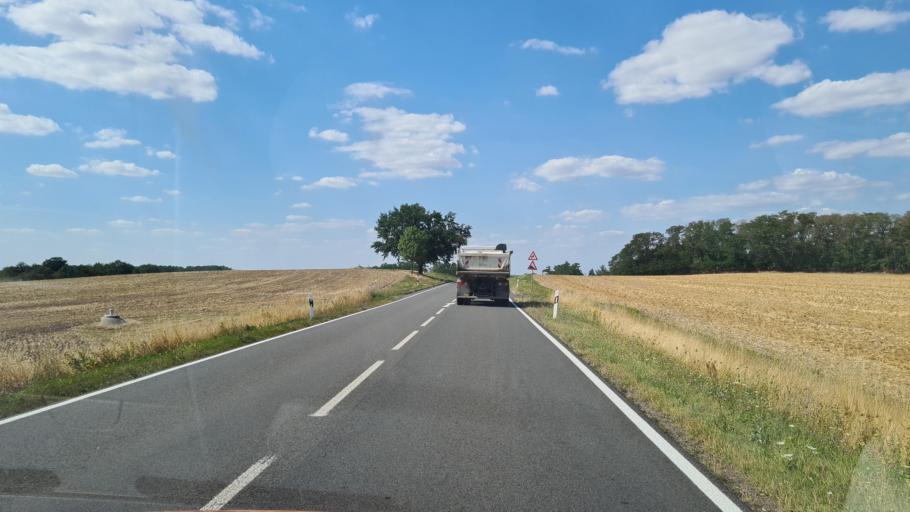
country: DE
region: Saxony
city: Eilenburg
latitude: 51.4292
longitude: 12.6276
